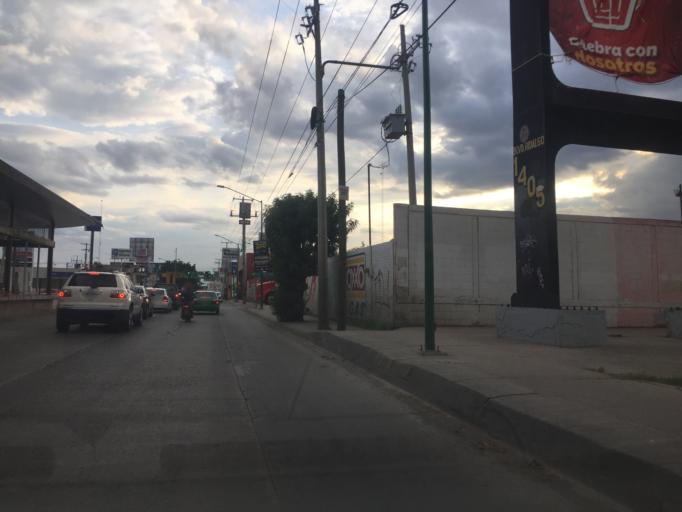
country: MX
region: Guanajuato
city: Leon
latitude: 21.1478
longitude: -101.6717
